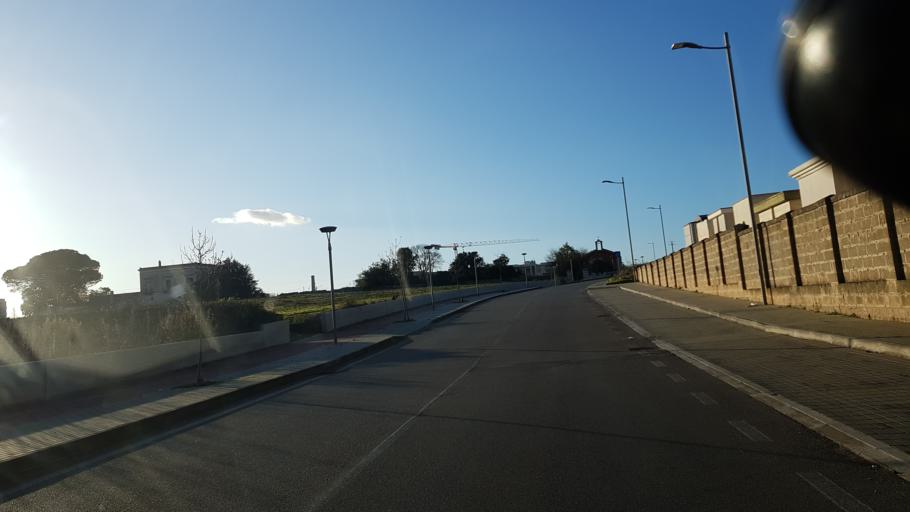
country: IT
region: Apulia
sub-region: Provincia di Bari
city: Gioia del Colle
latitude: 40.8013
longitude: 16.9102
